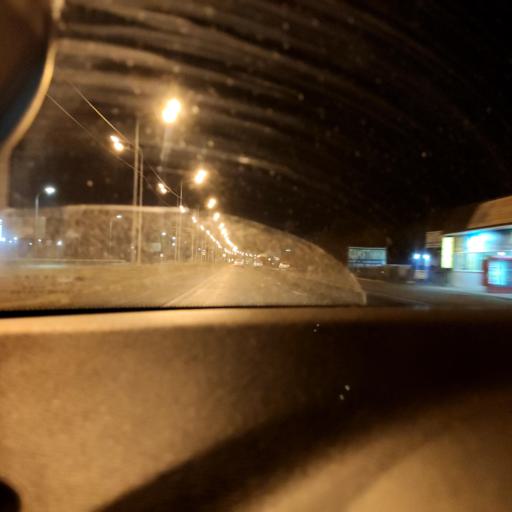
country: RU
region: Samara
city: Smyshlyayevka
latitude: 53.2620
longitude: 50.3821
